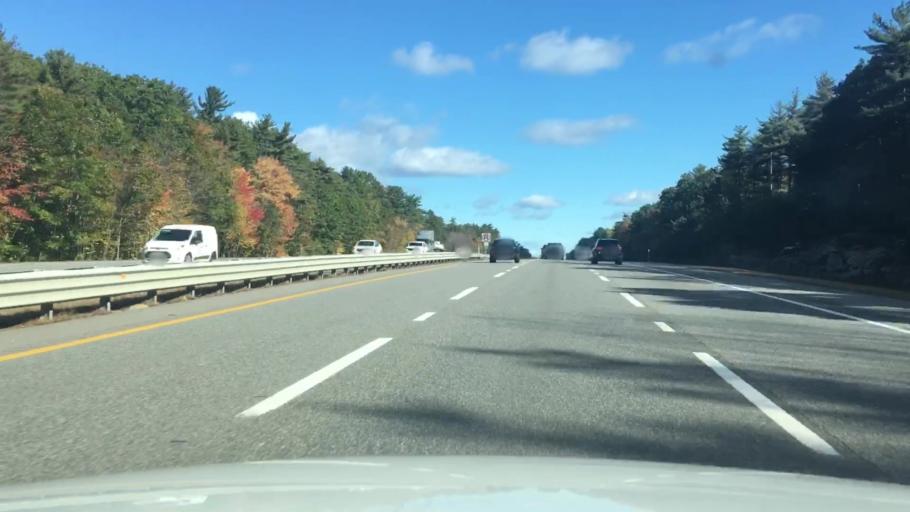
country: US
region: Maine
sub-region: York County
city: Ogunquit
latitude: 43.2406
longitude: -70.6299
